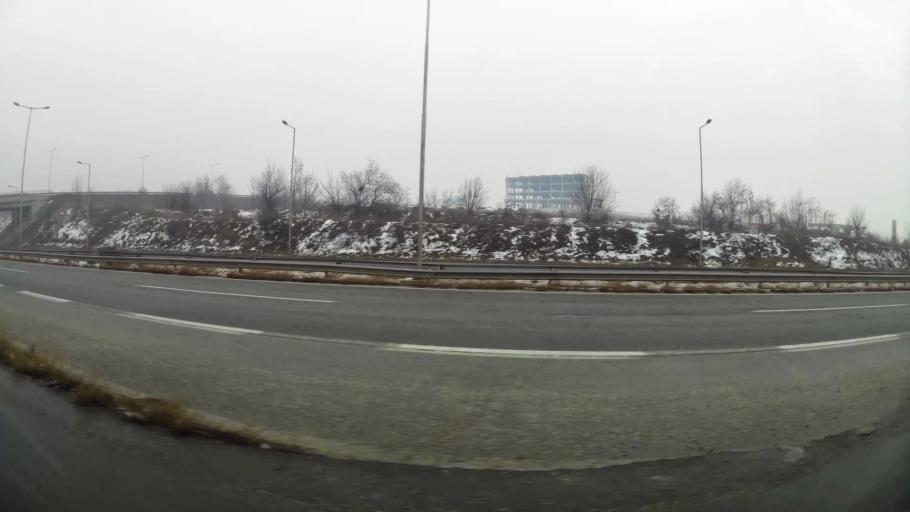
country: MK
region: Petrovec
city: Petrovec
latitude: 41.9582
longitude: 21.6315
